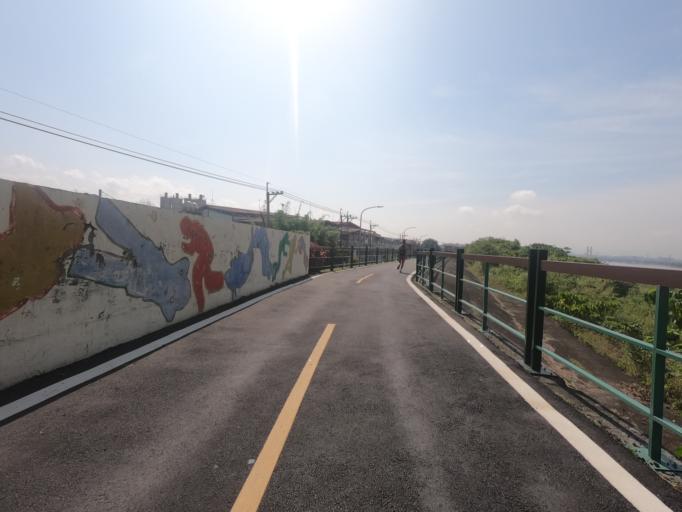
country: TW
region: Taipei
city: Taipei
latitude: 25.1000
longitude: 121.4889
